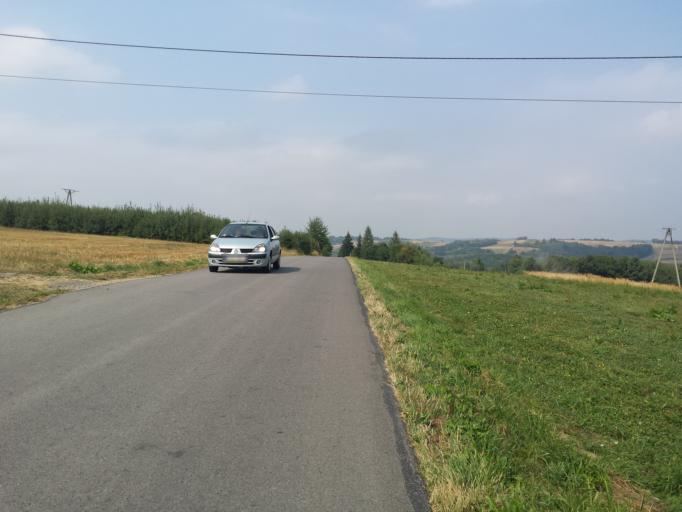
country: PL
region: Subcarpathian Voivodeship
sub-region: Powiat rzeszowski
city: Dynow
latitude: 49.8249
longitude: 22.2057
